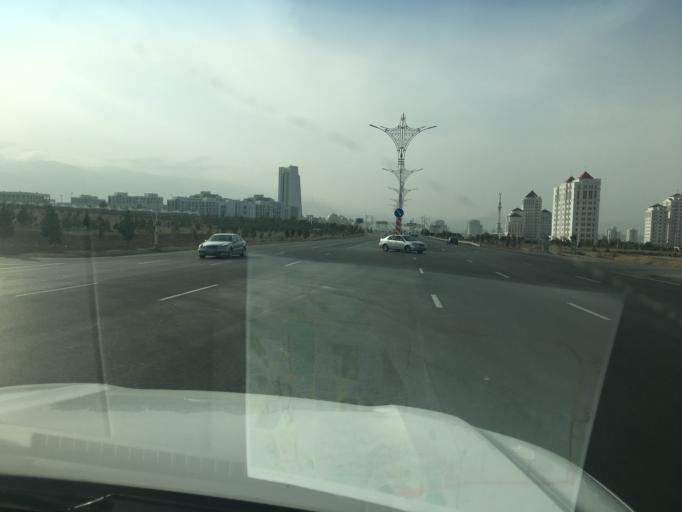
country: TM
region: Ahal
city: Ashgabat
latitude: 37.8788
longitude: 58.3989
